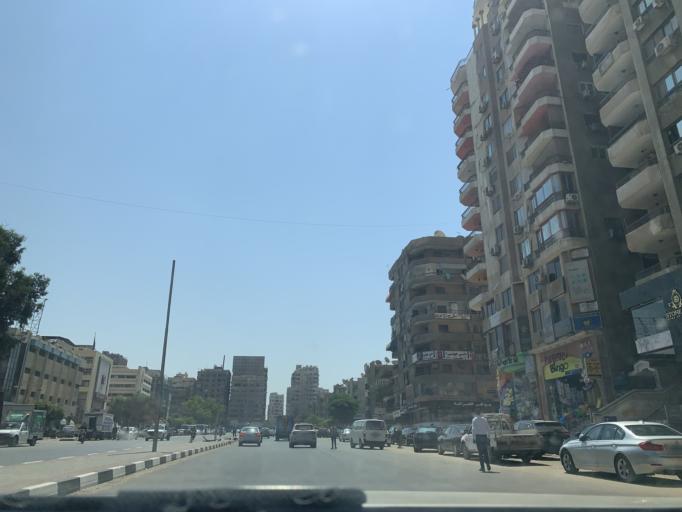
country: EG
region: Muhafazat al Qahirah
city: Cairo
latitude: 30.0519
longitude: 31.3465
